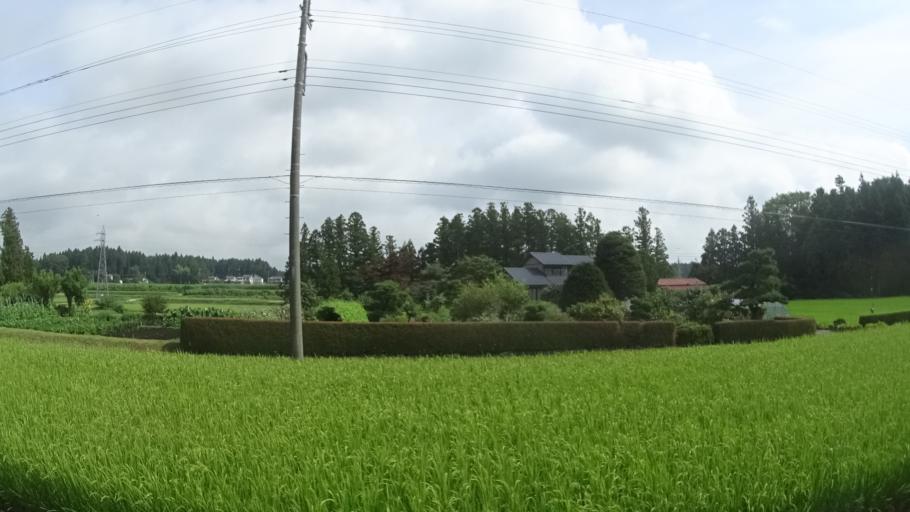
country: JP
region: Tochigi
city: Imaichi
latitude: 36.7029
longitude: 139.7119
